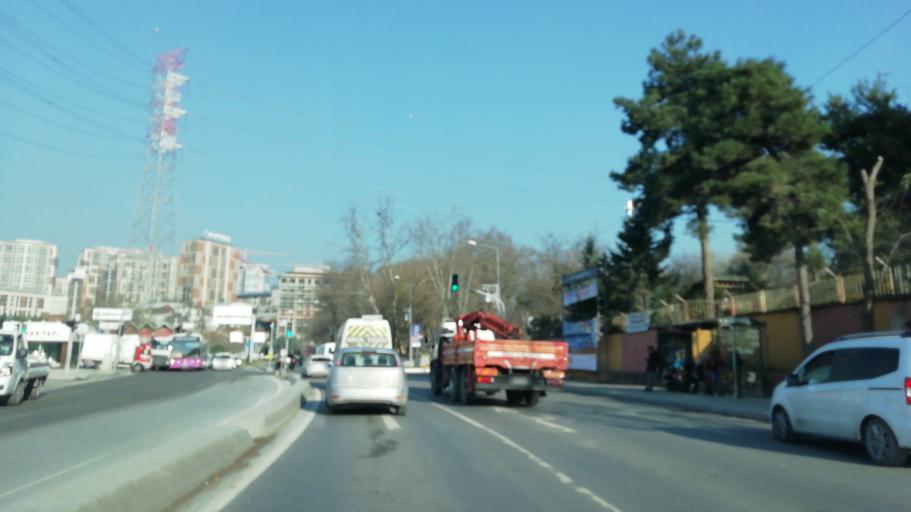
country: TR
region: Istanbul
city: Sisli
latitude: 41.0832
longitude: 28.9521
